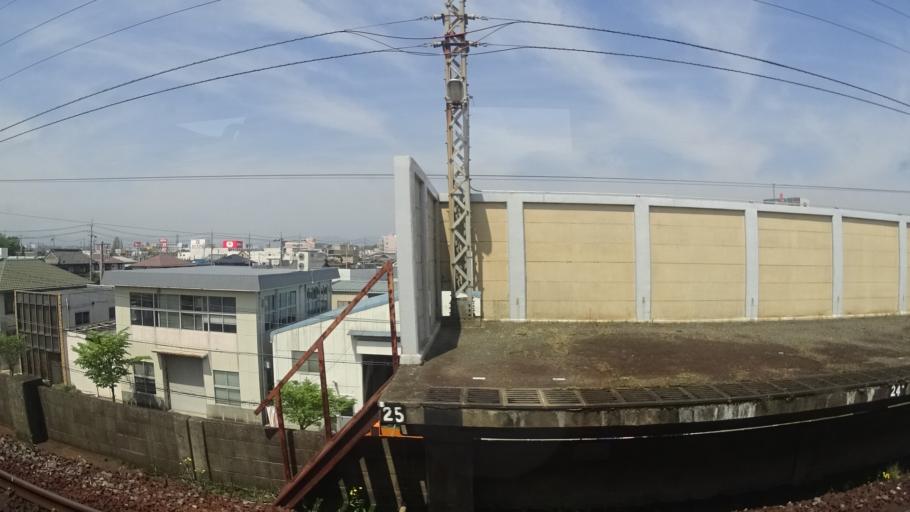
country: JP
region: Mie
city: Suzuka
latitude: 34.8771
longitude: 136.5883
